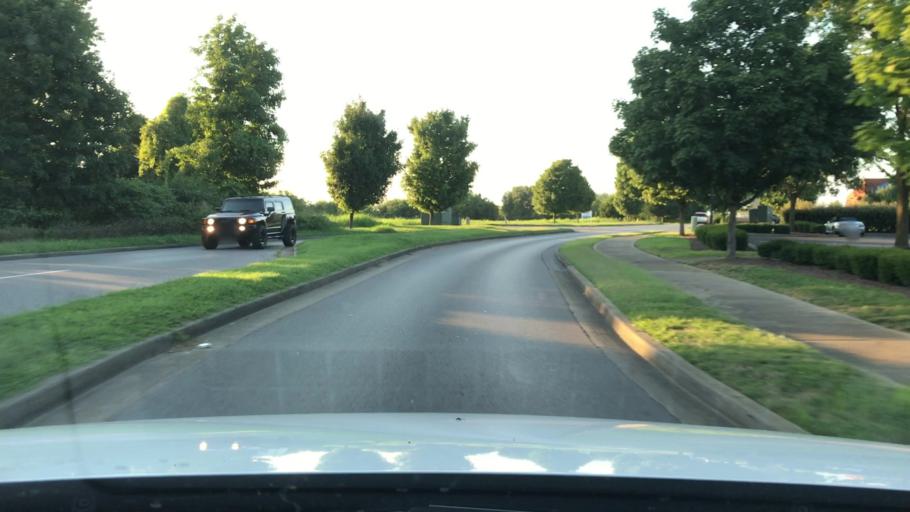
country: US
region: Tennessee
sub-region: Sumner County
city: Hendersonville
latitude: 36.3136
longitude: -86.5958
